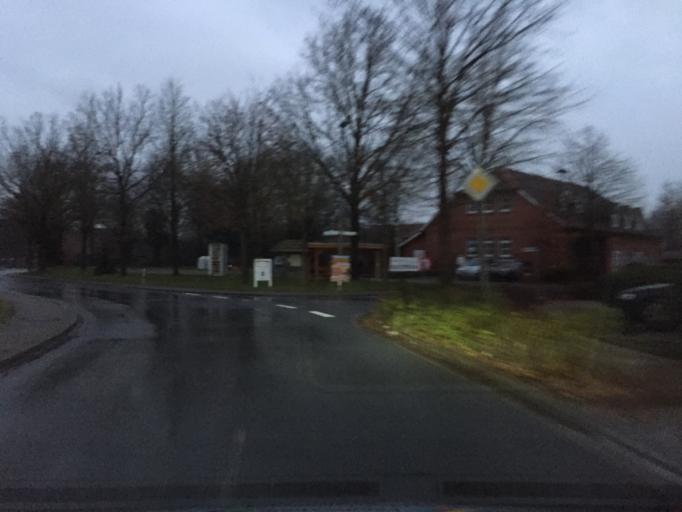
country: DE
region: Lower Saxony
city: Sudwalde
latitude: 52.7966
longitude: 8.8404
